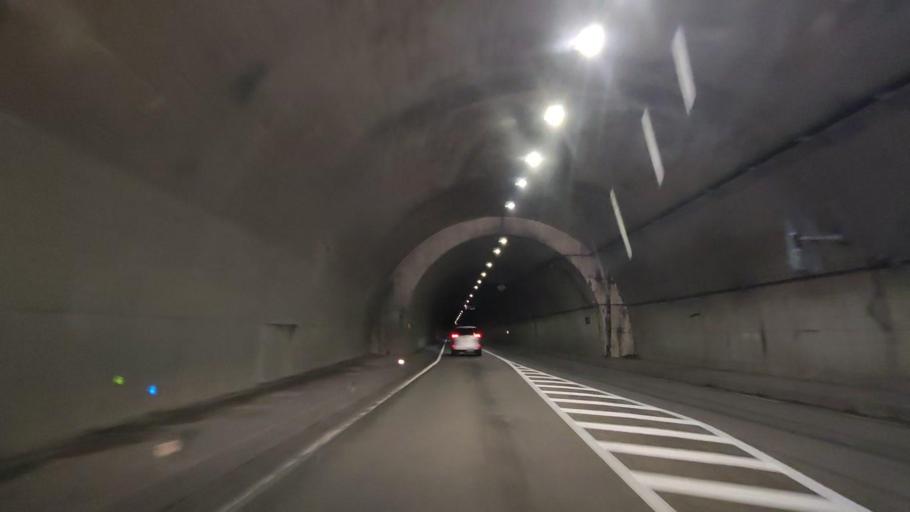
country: JP
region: Nagano
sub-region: Kitaazumi Gun
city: Hakuba
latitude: 36.8123
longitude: 137.9112
